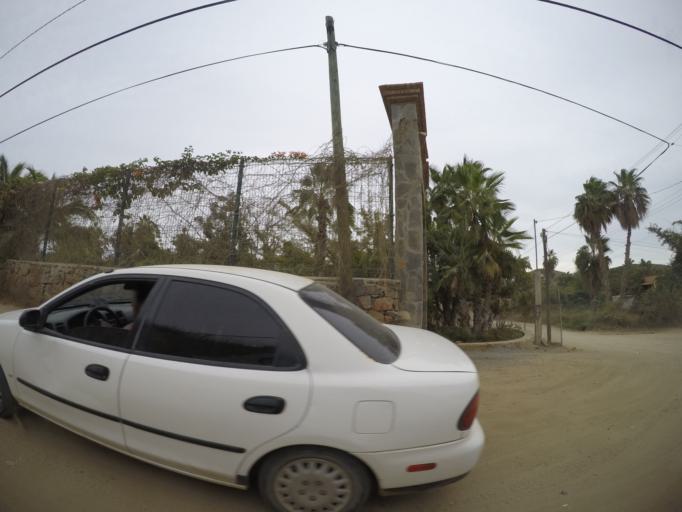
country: MX
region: Baja California Sur
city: Todos Santos
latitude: 23.4394
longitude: -110.2277
